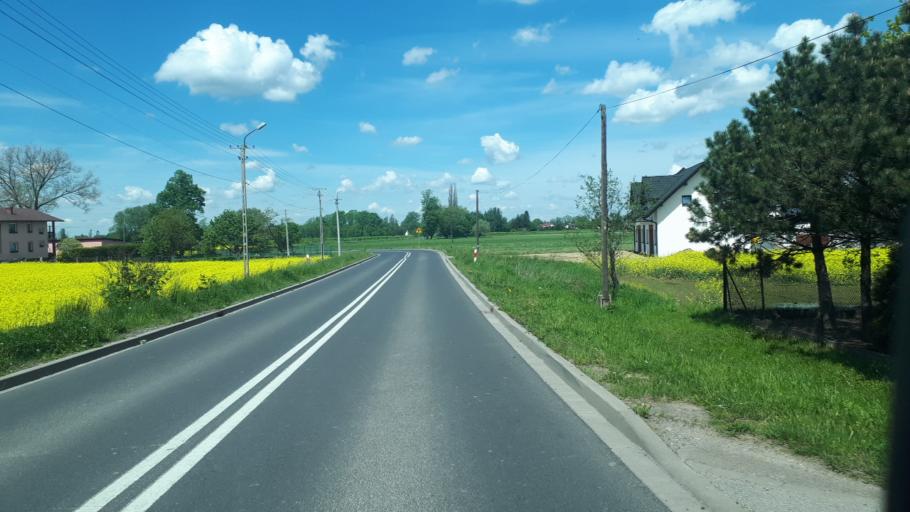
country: PL
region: Silesian Voivodeship
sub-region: Powiat bielski
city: Mazancowice
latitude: 49.8713
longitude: 18.9605
